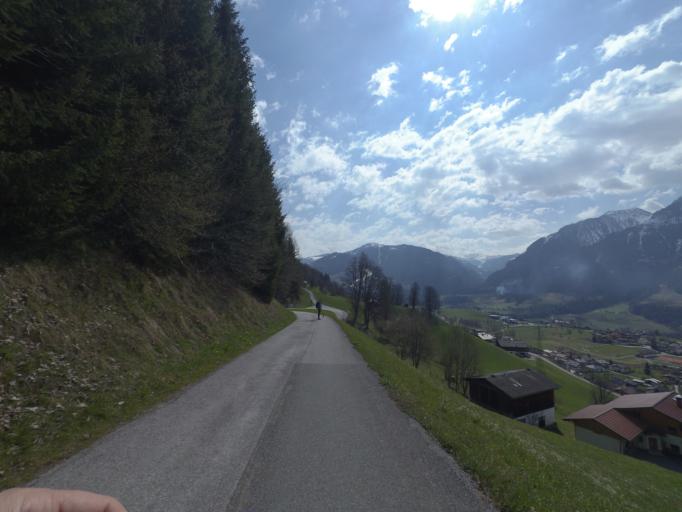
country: AT
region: Salzburg
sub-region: Politischer Bezirk Sankt Johann im Pongau
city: Sankt Veit im Pongau
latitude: 47.3358
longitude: 13.1529
